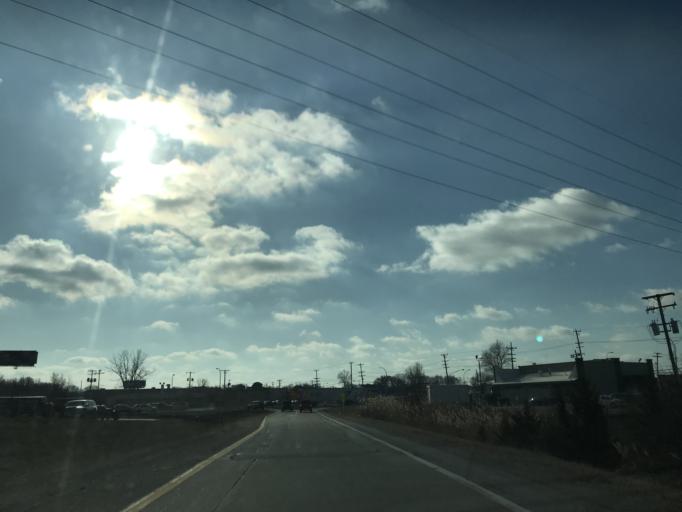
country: US
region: Michigan
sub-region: Oakland County
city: Madison Heights
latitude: 42.5058
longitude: -83.1163
